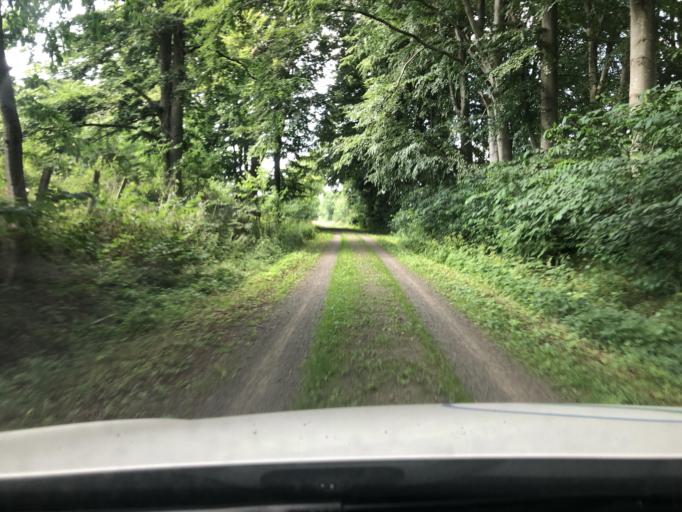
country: SE
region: Skane
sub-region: Kristianstads Kommun
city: Degeberga
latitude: 55.7861
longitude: 14.1719
